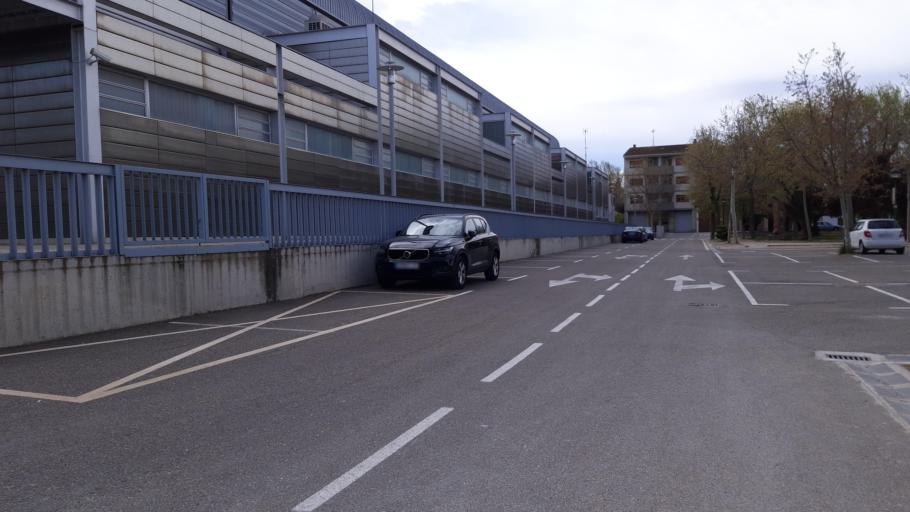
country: ES
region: Aragon
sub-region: Provincia de Zaragoza
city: Utebo
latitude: 41.7126
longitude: -1.0017
